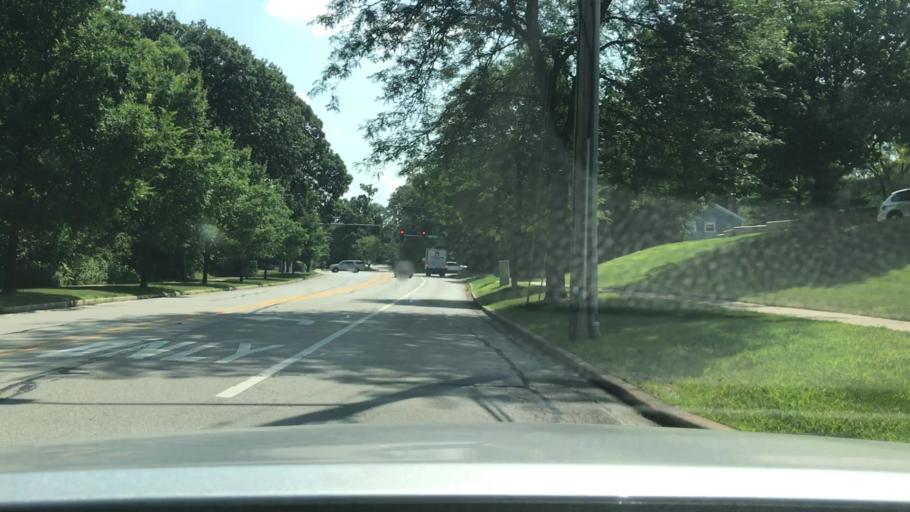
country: US
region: Illinois
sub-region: DuPage County
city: Naperville
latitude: 41.7404
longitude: -88.1195
